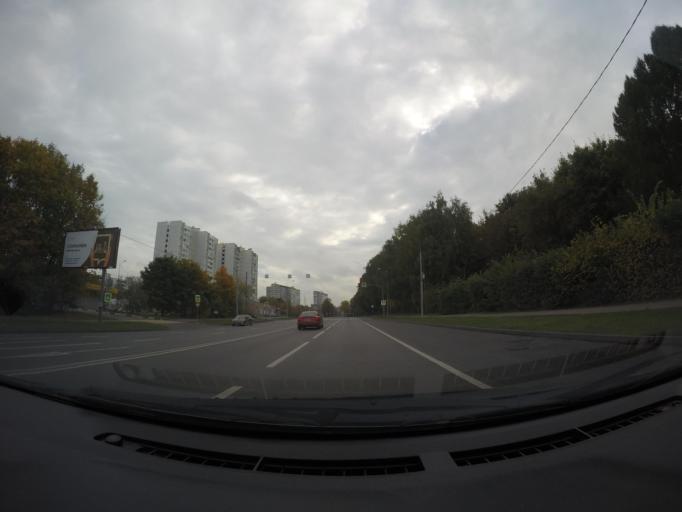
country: RU
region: Moscow
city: Ivanovskoye
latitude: 55.7705
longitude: 37.8203
